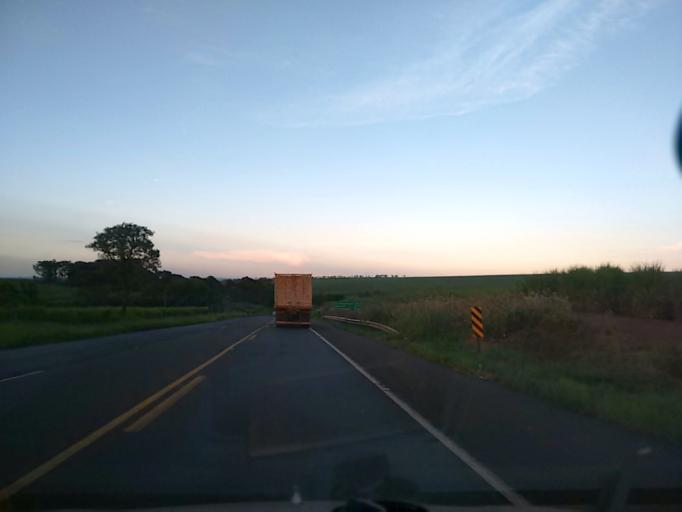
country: BR
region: Sao Paulo
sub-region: Jau
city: Jau
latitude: -22.1498
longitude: -48.4692
